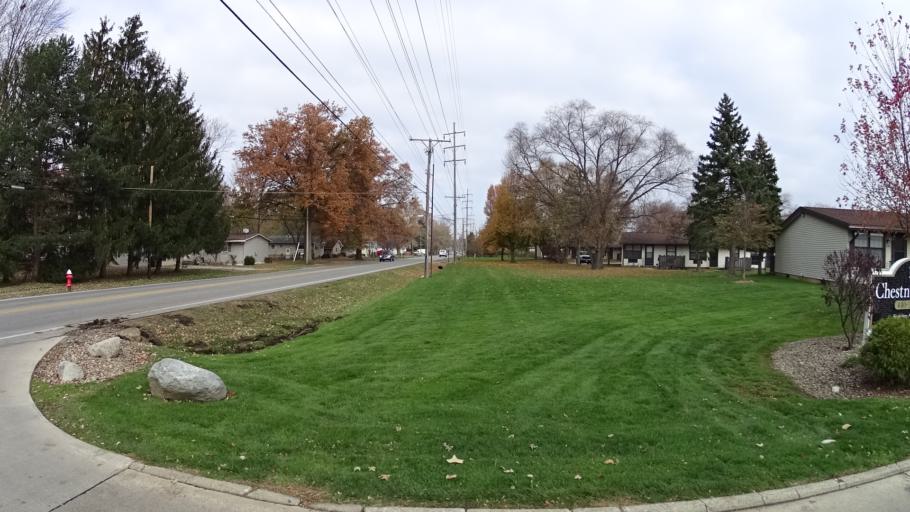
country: US
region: Ohio
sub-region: Lorain County
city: Elyria
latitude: 41.3588
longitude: -82.0780
